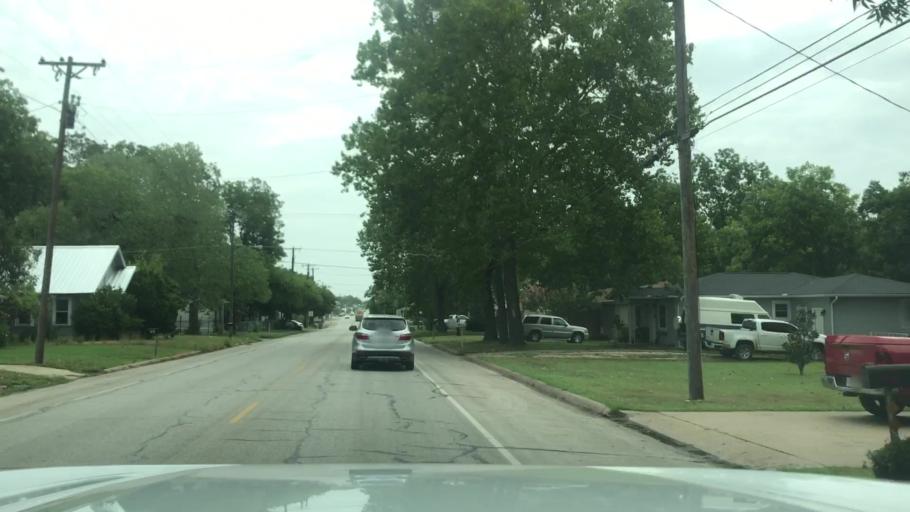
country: US
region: Texas
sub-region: Erath County
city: Dublin
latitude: 32.0861
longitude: -98.3464
